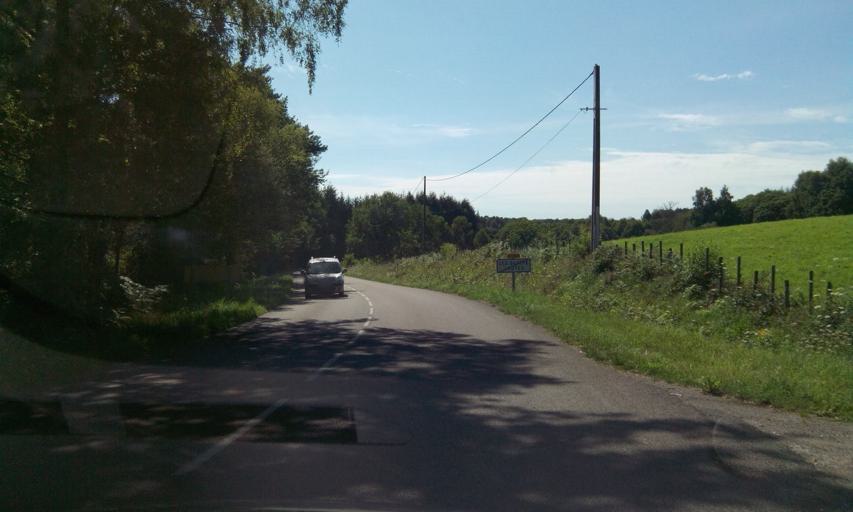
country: FR
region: Limousin
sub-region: Departement de la Correze
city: Beynat
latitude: 45.1367
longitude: 1.7782
